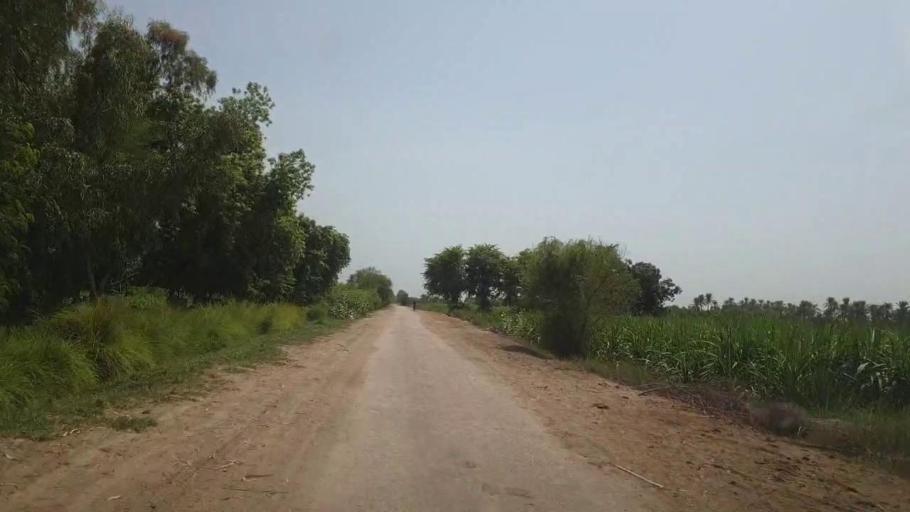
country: PK
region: Sindh
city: Sobhadero
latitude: 27.4427
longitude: 68.4037
